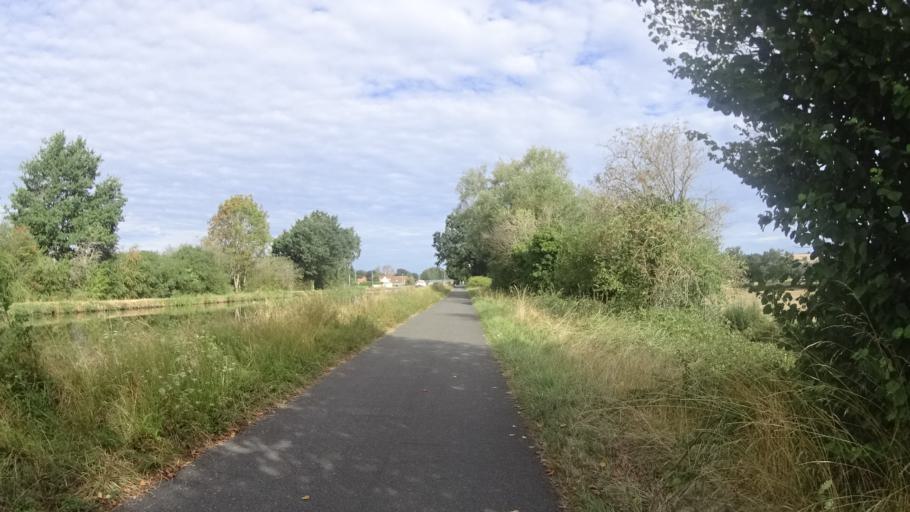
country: FR
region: Auvergne
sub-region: Departement de l'Allier
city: Diou
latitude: 46.5232
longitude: 3.7778
